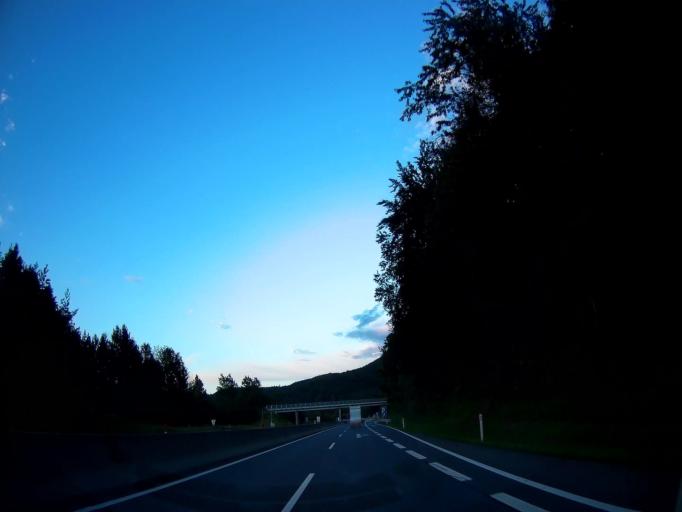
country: AT
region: Lower Austria
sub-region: Politischer Bezirk Sankt Polten
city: Eichgraben
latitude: 48.1615
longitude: 16.0024
